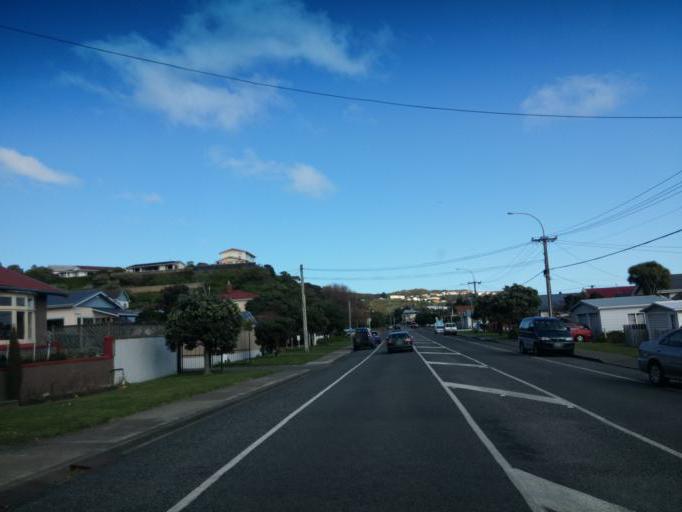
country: NZ
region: Wellington
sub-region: Wellington City
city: Wellington
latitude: -41.3203
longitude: 174.8203
